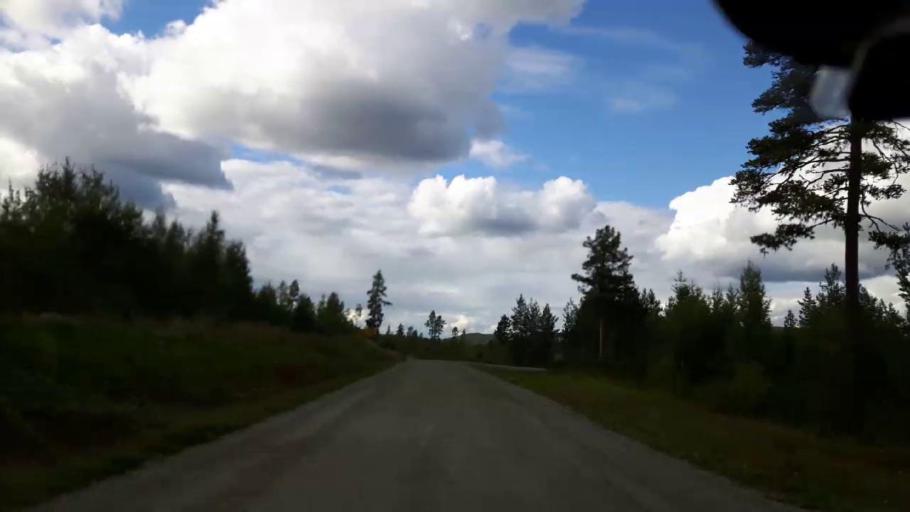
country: SE
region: Jaemtland
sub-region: Stroemsunds Kommun
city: Stroemsund
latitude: 63.4041
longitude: 15.5681
